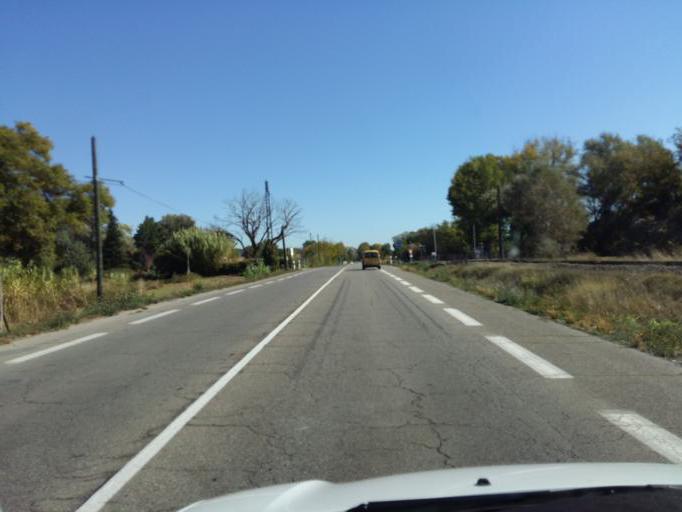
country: FR
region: Provence-Alpes-Cote d'Azur
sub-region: Departement du Vaucluse
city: Lauris
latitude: 43.7486
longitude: 5.2862
